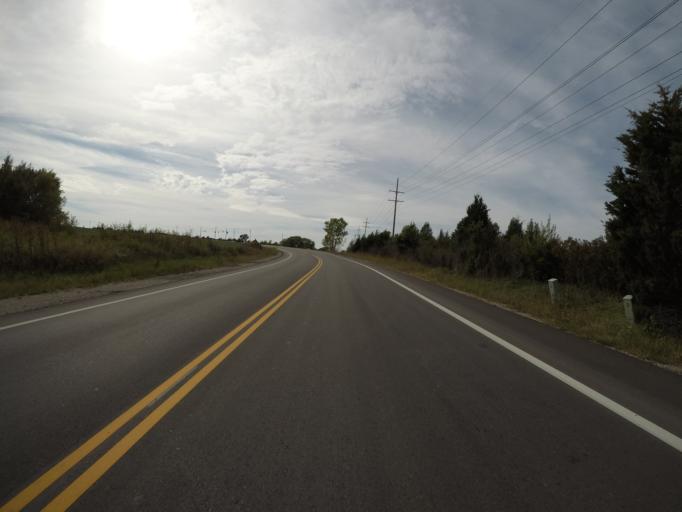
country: US
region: Kansas
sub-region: Johnson County
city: Olathe
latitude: 38.8546
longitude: -94.8676
